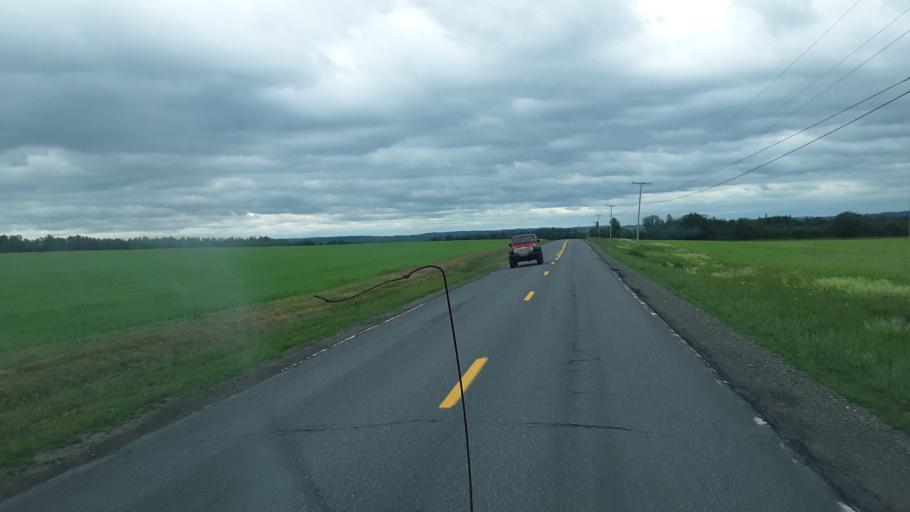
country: US
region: Maine
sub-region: Aroostook County
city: Presque Isle
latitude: 46.7486
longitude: -68.1753
